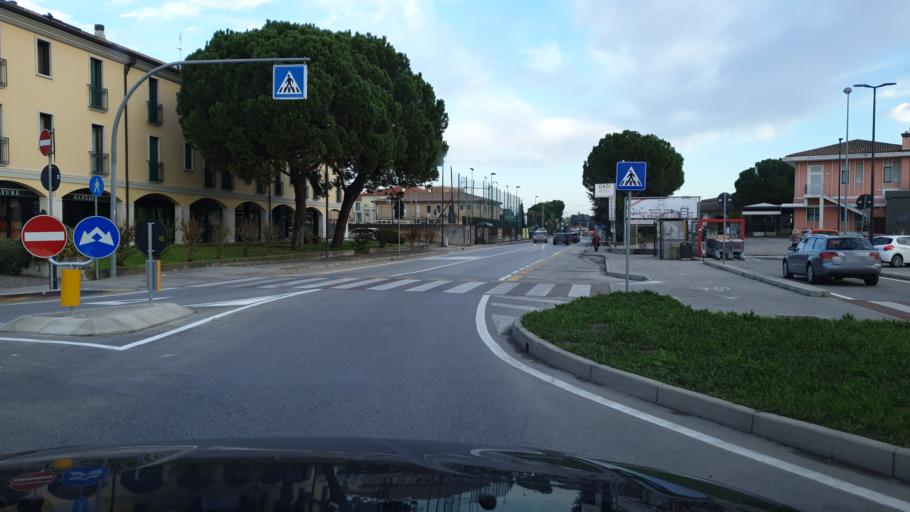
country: IT
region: Veneto
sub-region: Provincia di Padova
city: Conselve
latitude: 45.2322
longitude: 11.8700
